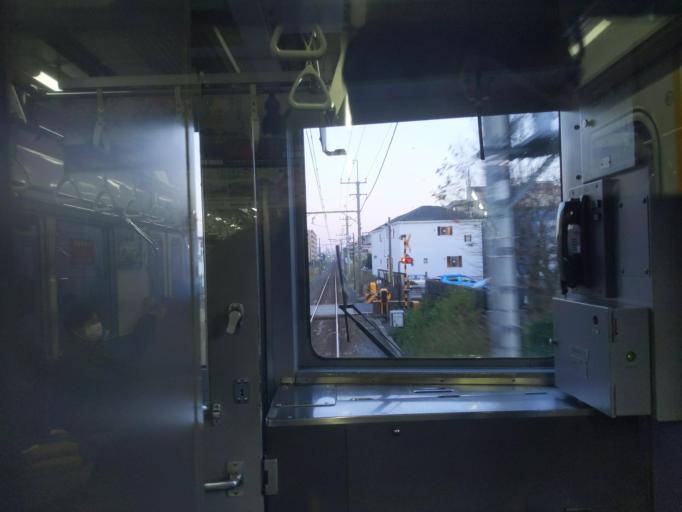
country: JP
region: Chiba
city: Noda
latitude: 35.9223
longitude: 139.9002
